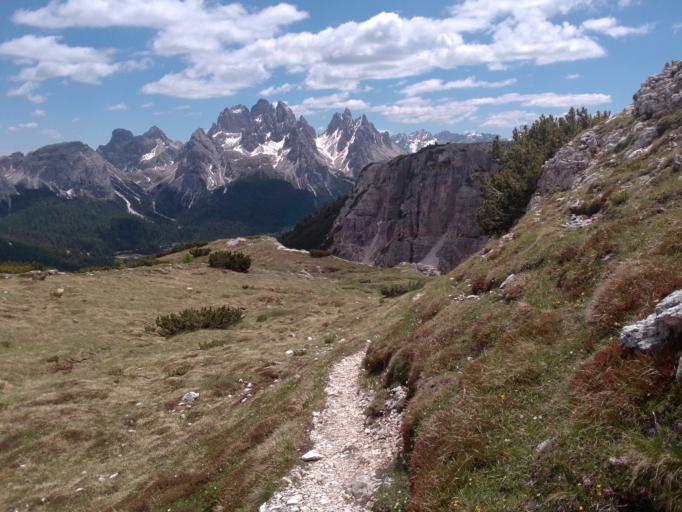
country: IT
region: Trentino-Alto Adige
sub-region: Bolzano
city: Dobbiaco
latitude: 46.6221
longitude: 12.2491
